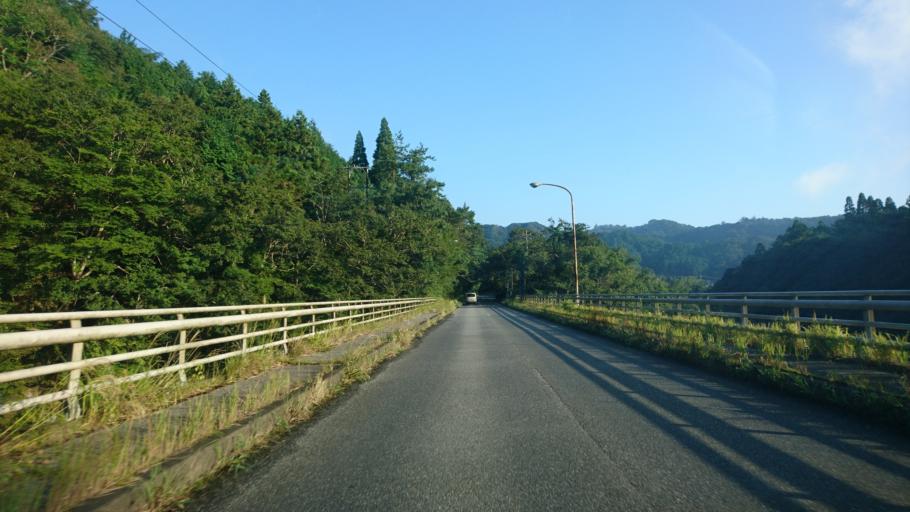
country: JP
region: Chiba
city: Kawaguchi
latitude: 35.1861
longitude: 140.0079
